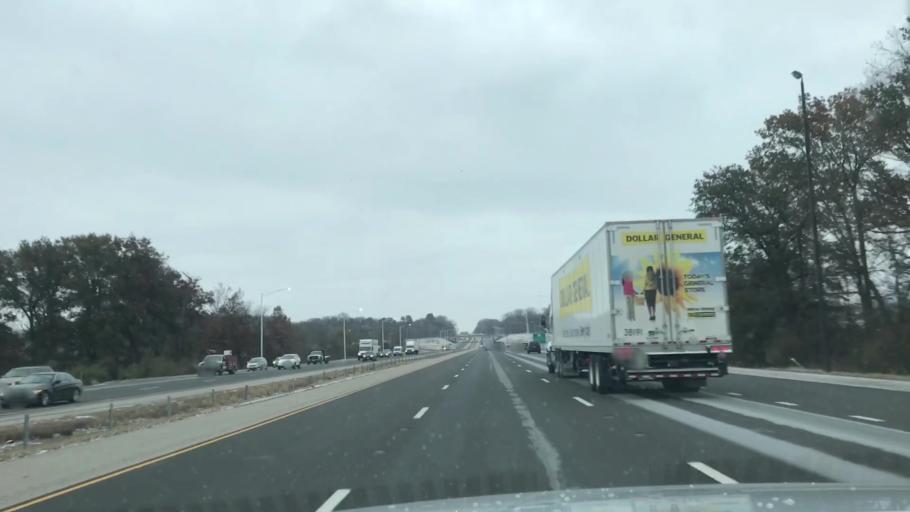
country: US
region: Illinois
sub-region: Madison County
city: Glen Carbon
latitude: 38.7567
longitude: -90.0183
